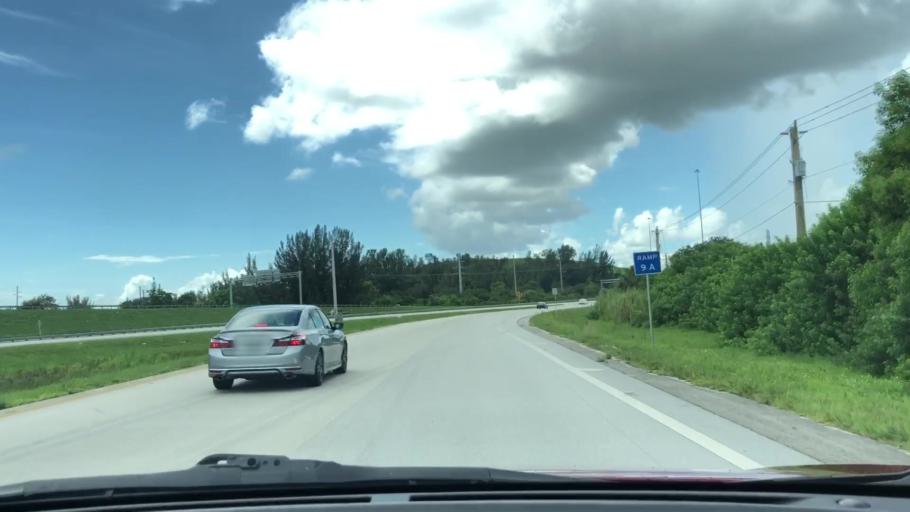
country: US
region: Florida
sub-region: Broward County
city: Broadview Park
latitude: 26.0820
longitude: -80.2047
